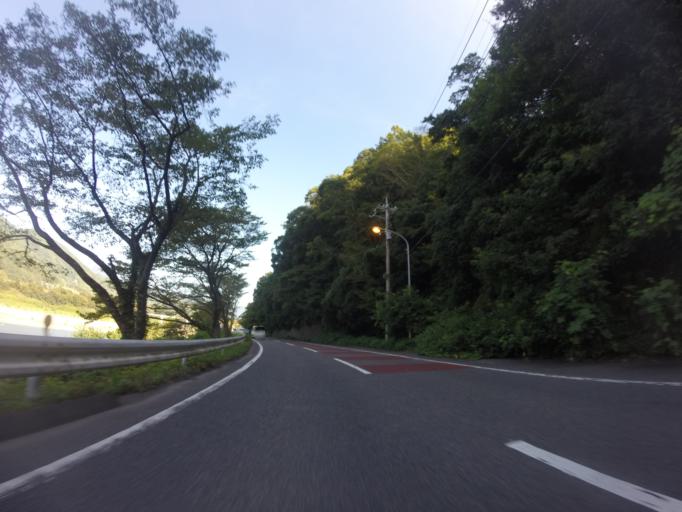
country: JP
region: Shizuoka
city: Fujinomiya
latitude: 35.3015
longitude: 138.4571
